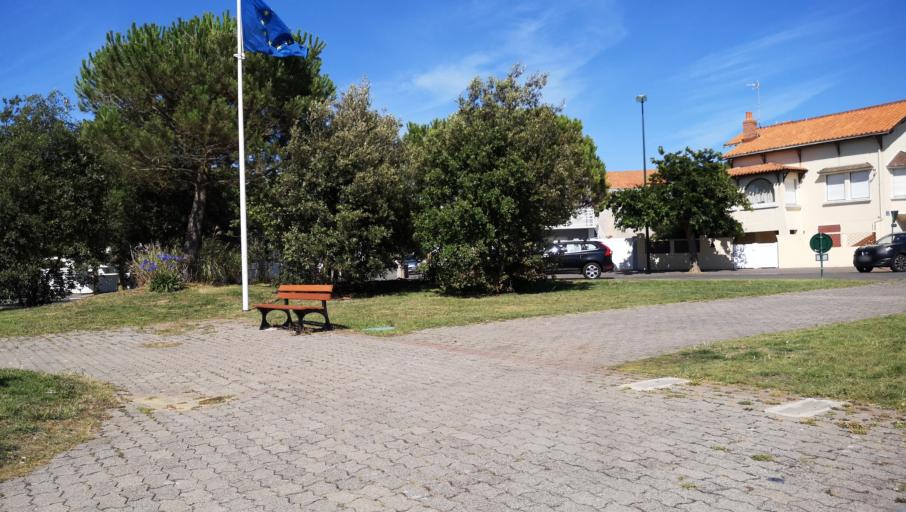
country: FR
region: Pays de la Loire
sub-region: Departement de la Vendee
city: Les Sables-d'Olonne
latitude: 46.4877
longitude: -1.7653
